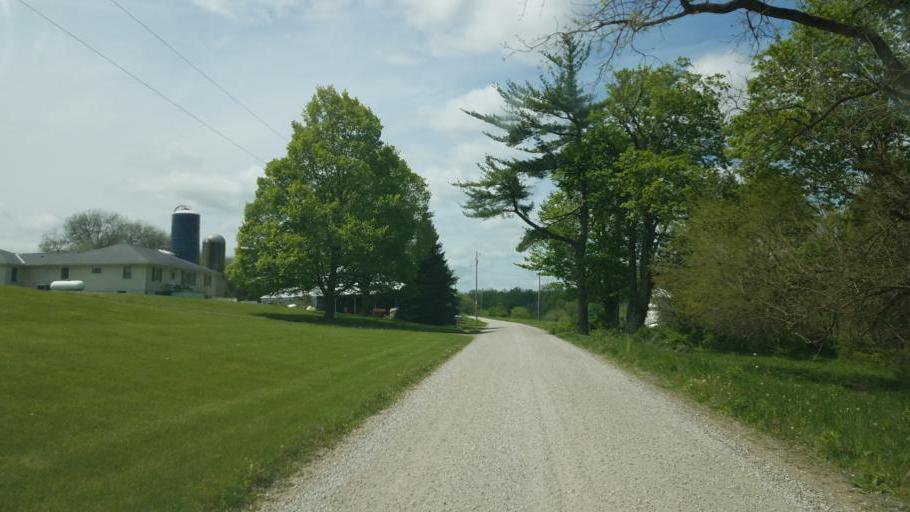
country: US
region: Ohio
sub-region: Richland County
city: Lexington
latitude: 40.5676
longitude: -82.6536
